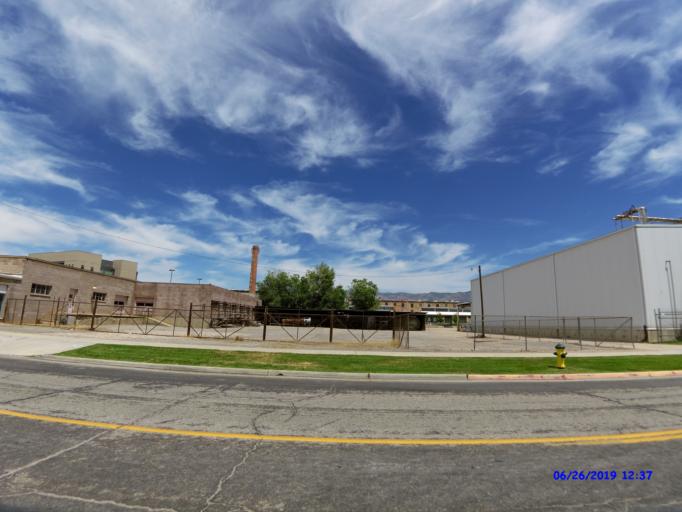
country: US
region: Utah
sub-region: Weber County
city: Ogden
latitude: 41.2291
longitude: -111.9748
